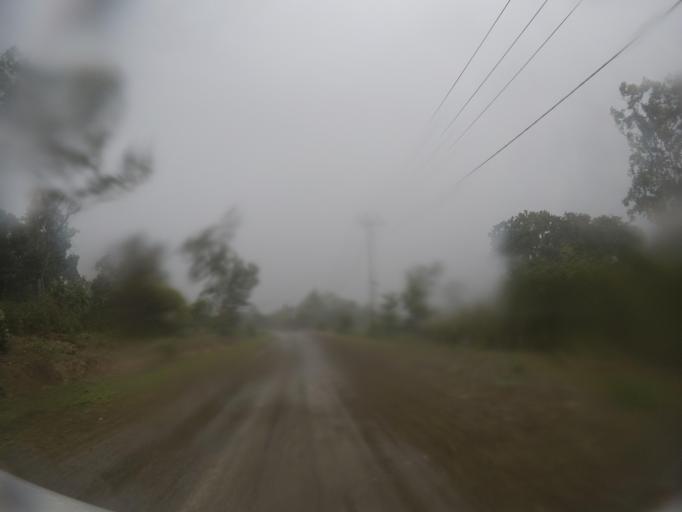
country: TL
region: Bobonaro
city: Maliana
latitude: -8.8594
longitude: 125.0874
